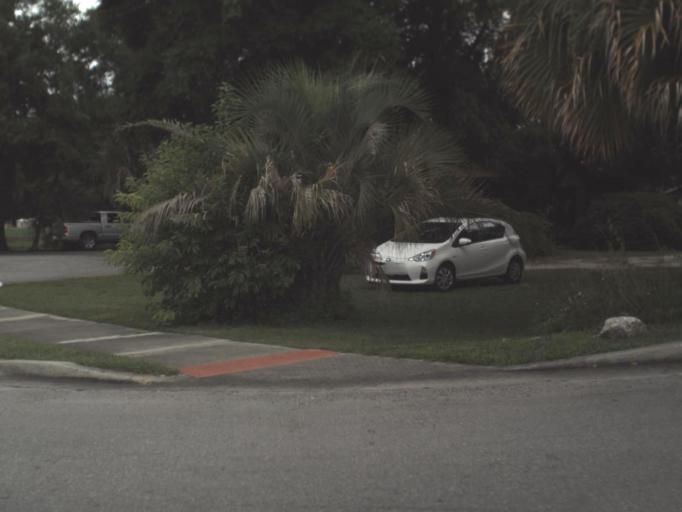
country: US
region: Florida
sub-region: Levy County
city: Williston
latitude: 29.3851
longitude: -82.4559
